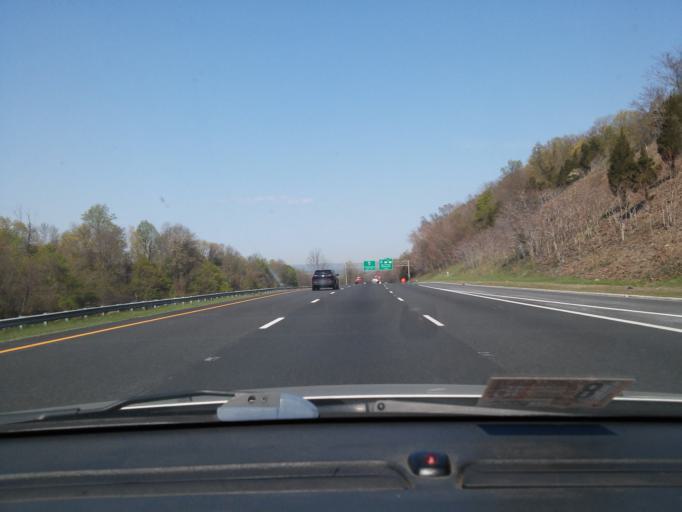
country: US
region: New Jersey
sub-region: Somerset County
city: Green Knoll
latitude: 40.6431
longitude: -74.6172
